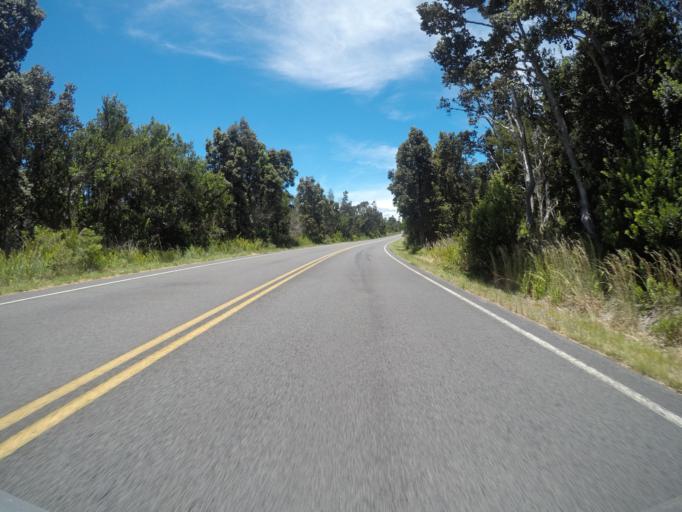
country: US
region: Hawaii
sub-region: Hawaii County
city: Volcano
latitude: 19.3509
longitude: -155.2192
